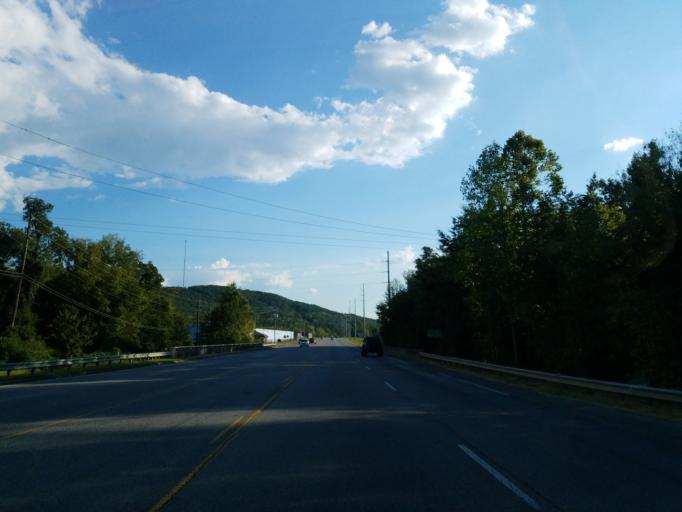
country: US
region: Georgia
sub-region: Murray County
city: Chatsworth
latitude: 34.8198
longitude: -84.7645
